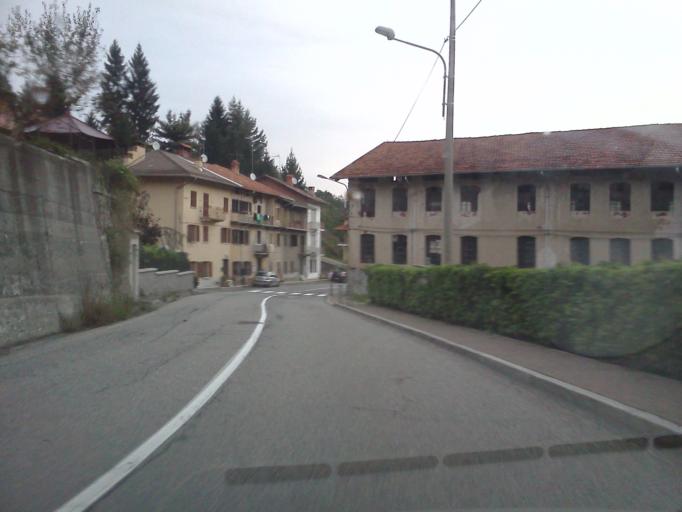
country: IT
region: Piedmont
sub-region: Provincia di Biella
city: Lanvario
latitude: 45.6546
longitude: 8.1950
